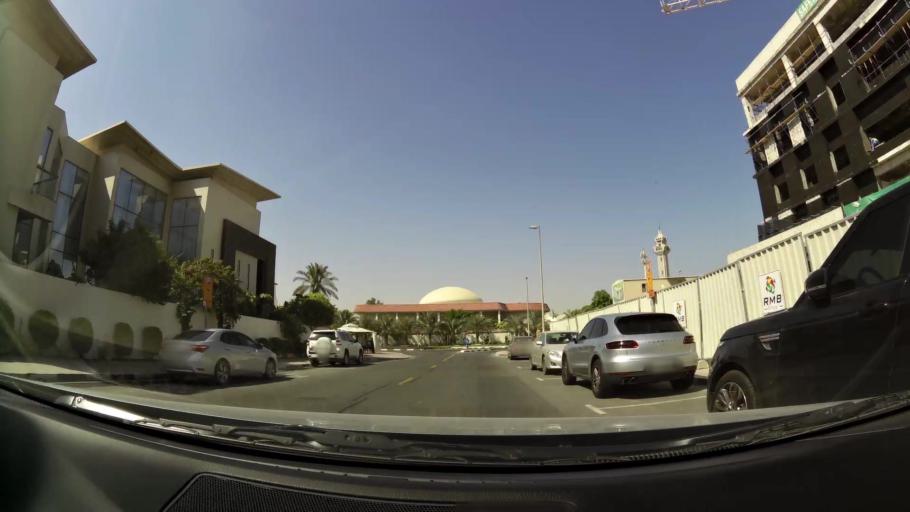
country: AE
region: Ash Shariqah
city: Sharjah
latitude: 25.2433
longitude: 55.2814
